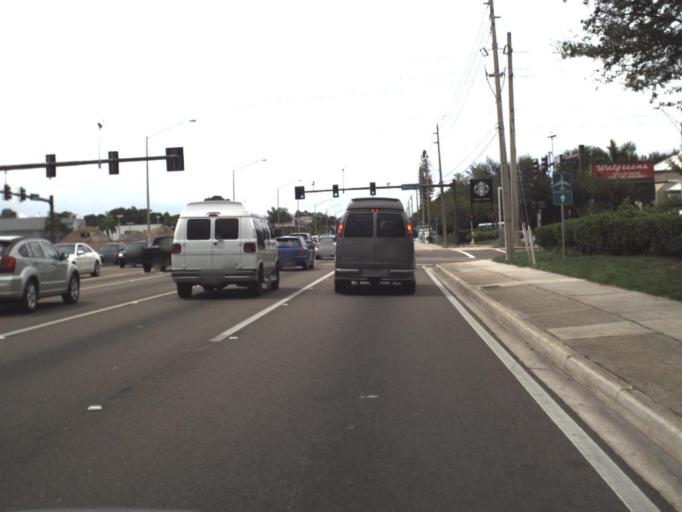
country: US
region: Florida
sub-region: Sarasota County
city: South Gate Ridge
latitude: 27.2989
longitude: -82.4968
